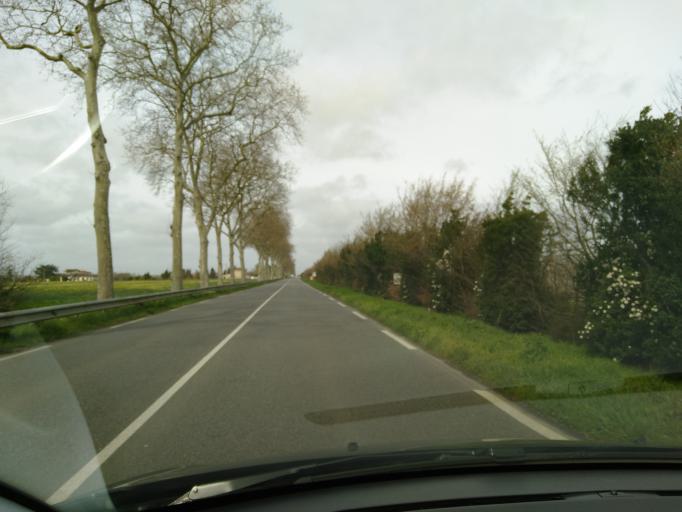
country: FR
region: Midi-Pyrenees
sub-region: Departement de la Haute-Garonne
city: Seilh
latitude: 43.7078
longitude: 1.3417
